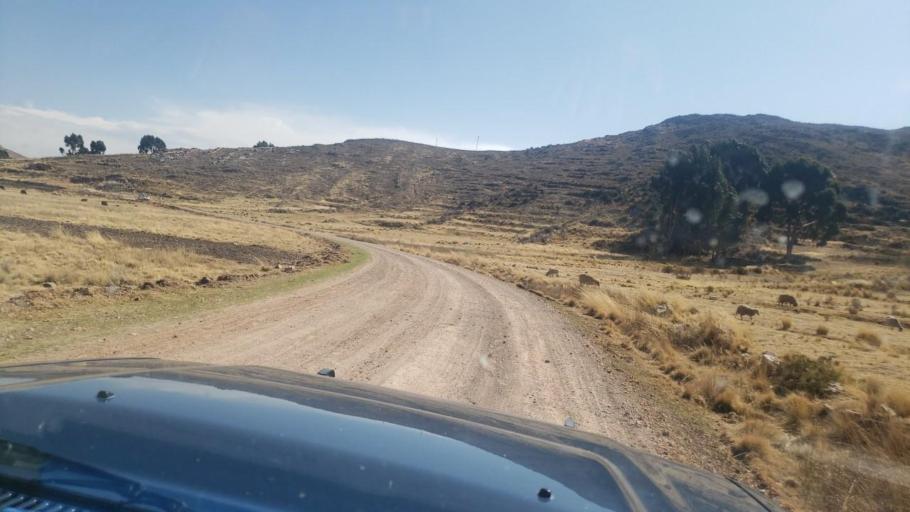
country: BO
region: La Paz
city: Huatajata
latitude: -16.3357
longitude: -68.6808
